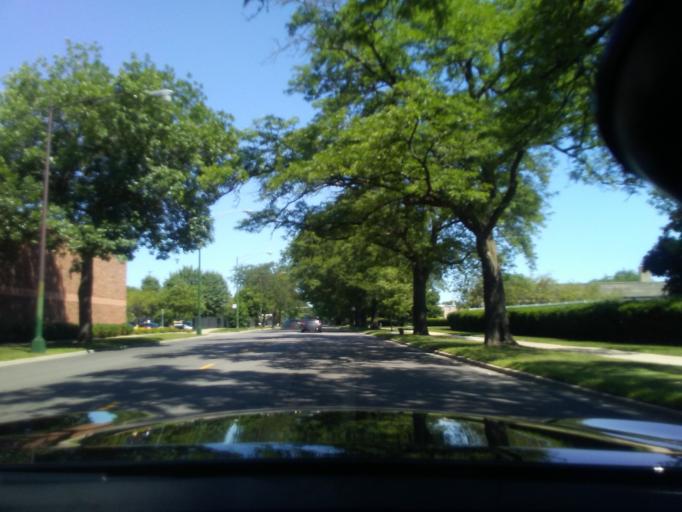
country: US
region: Illinois
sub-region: Cook County
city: Evanston
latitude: 42.0024
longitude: -87.6788
